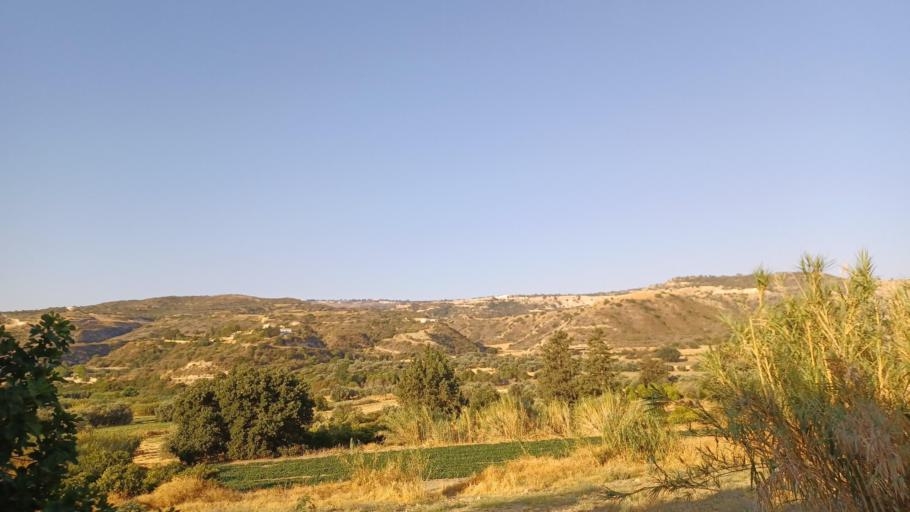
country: CY
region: Pafos
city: Polis
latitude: 35.0033
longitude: 32.4395
